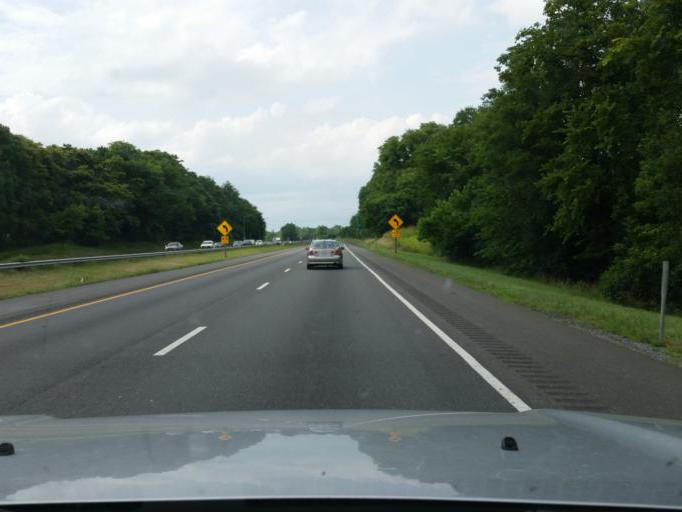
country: US
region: Maryland
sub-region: Frederick County
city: Urbana
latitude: 39.3175
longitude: -77.3525
